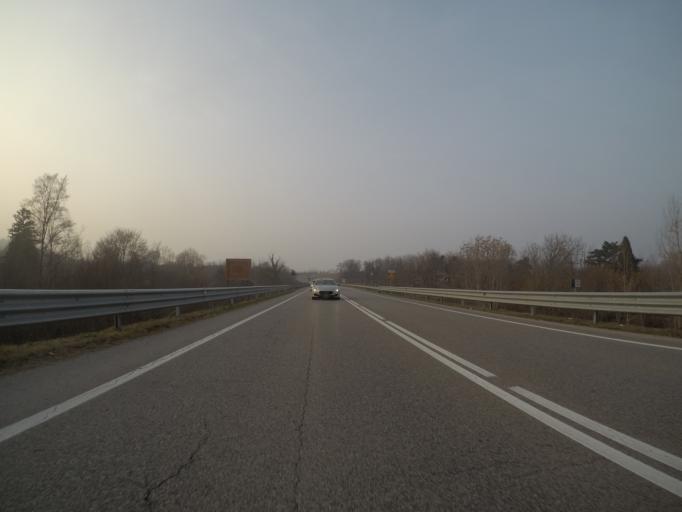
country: IT
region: Veneto
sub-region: Provincia di Treviso
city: Onigo
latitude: 45.8618
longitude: 11.9930
